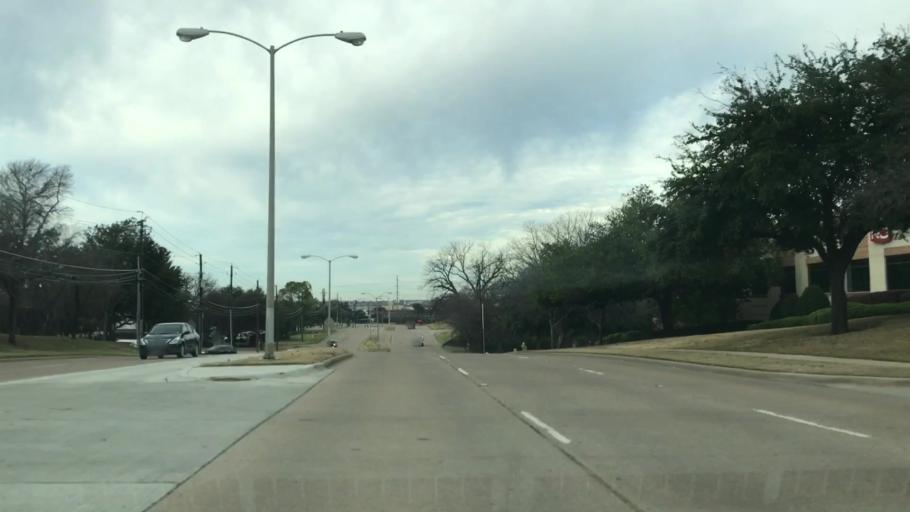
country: US
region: Texas
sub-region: Dallas County
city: University Park
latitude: 32.8370
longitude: -96.8678
